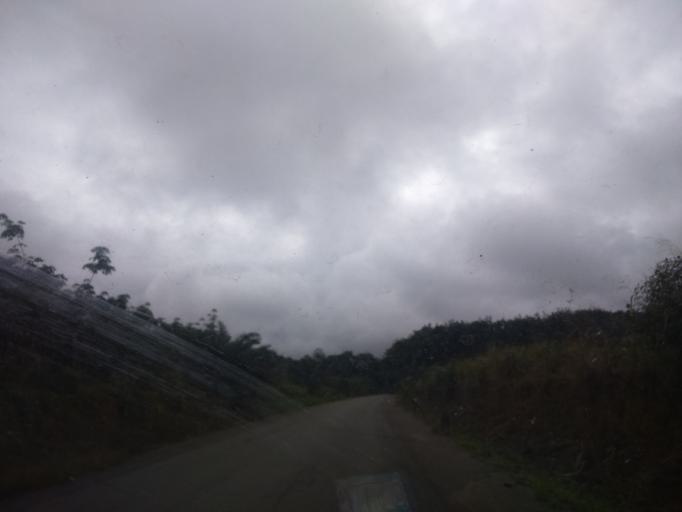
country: CI
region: Sud-Comoe
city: Bonoua
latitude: 5.2845
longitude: -3.4714
